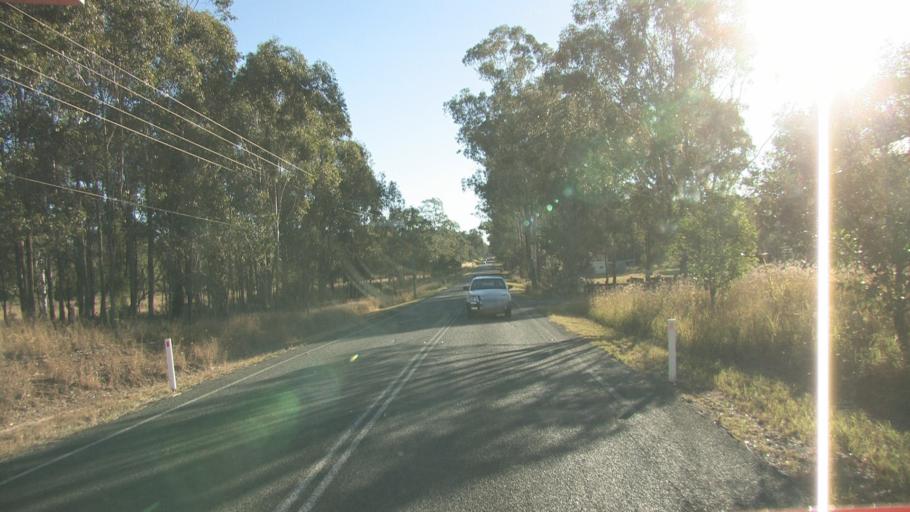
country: AU
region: Queensland
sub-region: Logan
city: North Maclean
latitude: -27.7595
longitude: 153.0430
